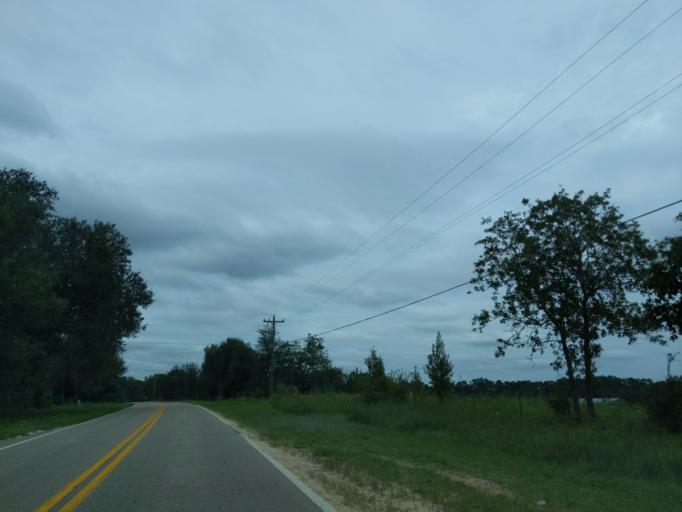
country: US
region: Florida
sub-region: Gadsden County
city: Midway
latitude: 30.4358
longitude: -84.4118
